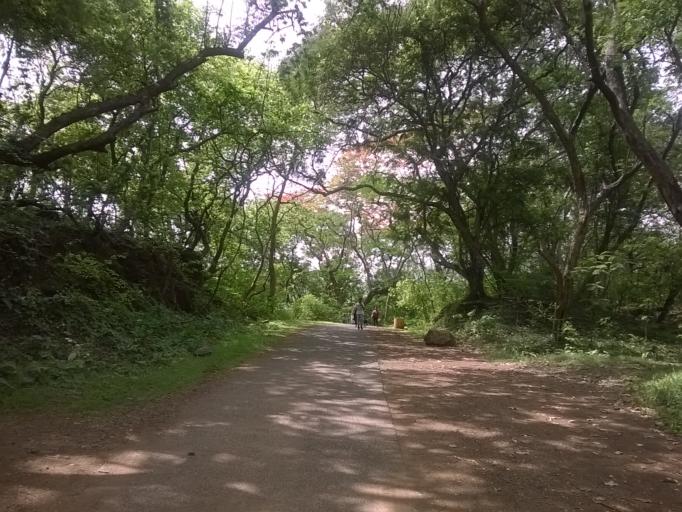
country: IN
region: Maharashtra
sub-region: Mumbai Suburban
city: Borivli
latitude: 19.2250
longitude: 72.8714
